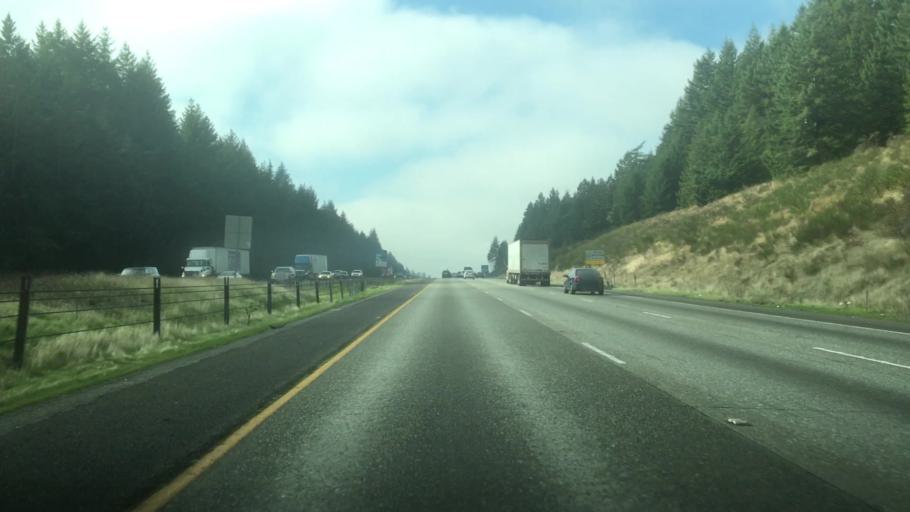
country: US
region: Washington
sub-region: Thurston County
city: Tanglewilde-Thompson Place
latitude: 47.0665
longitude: -122.7418
